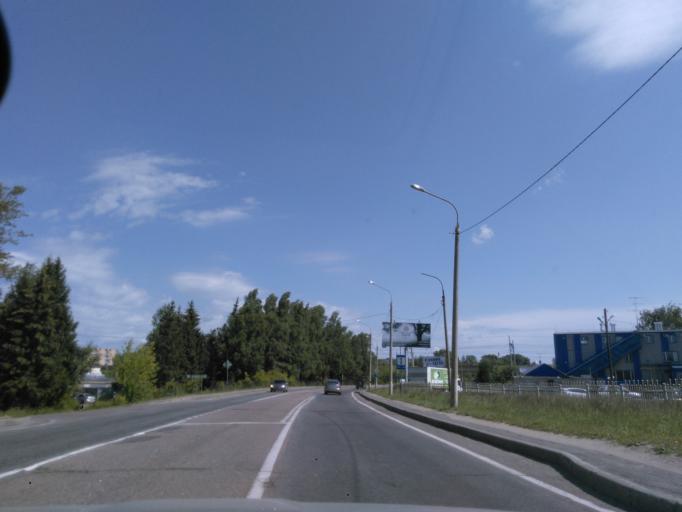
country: RU
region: Moskovskaya
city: Solnechnogorsk
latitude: 56.1862
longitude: 36.9625
